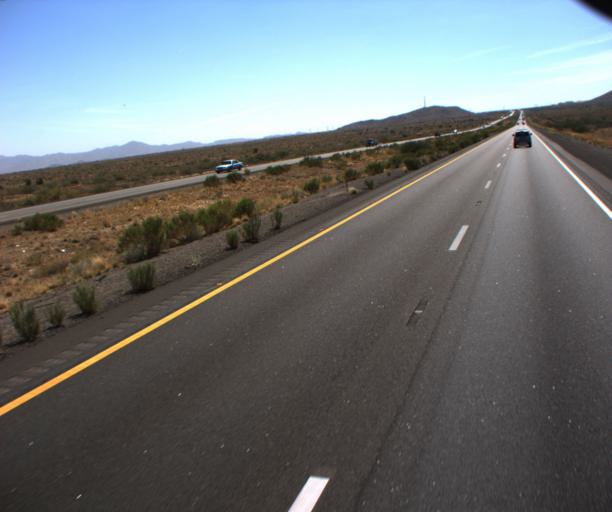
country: US
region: Arizona
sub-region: Mohave County
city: New Kingman-Butler
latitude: 35.2062
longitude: -113.9502
